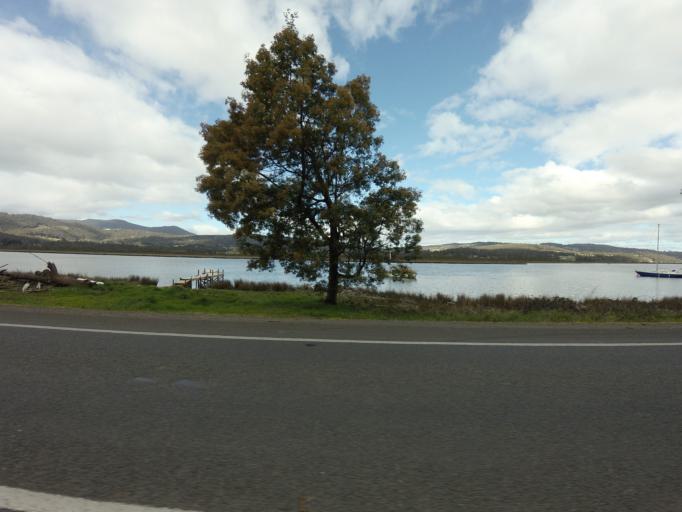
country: AU
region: Tasmania
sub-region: Huon Valley
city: Franklin
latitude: -43.1034
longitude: 147.0016
